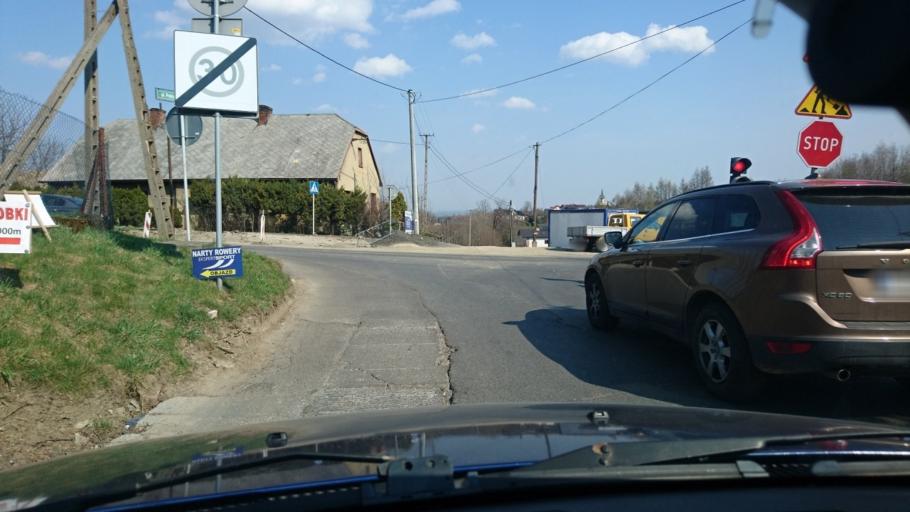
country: PL
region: Silesian Voivodeship
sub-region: Powiat bielski
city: Kozy
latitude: 49.8230
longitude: 19.1153
